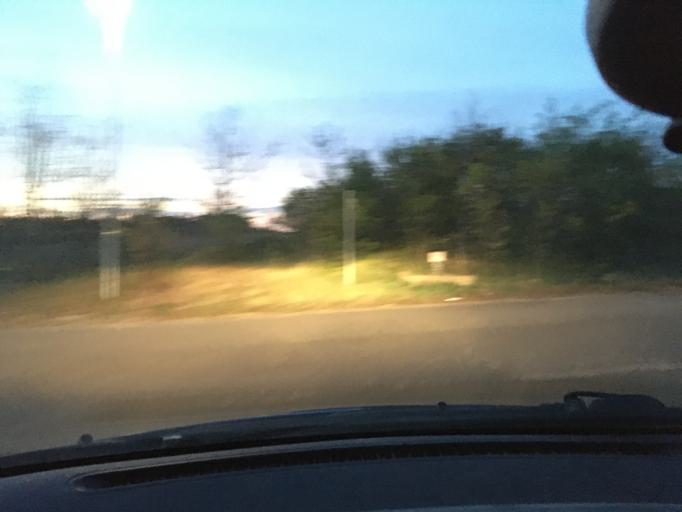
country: DE
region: Lower Saxony
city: Hanstedt
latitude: 53.2359
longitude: 10.0200
